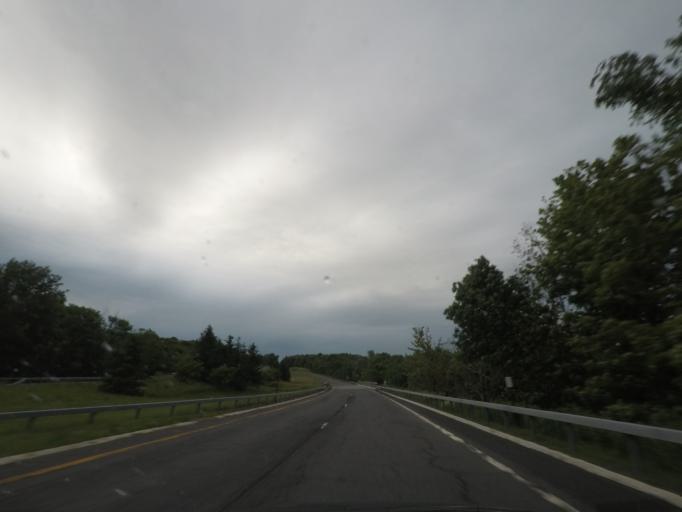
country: US
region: New York
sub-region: Columbia County
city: Chatham
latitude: 42.3320
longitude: -73.5679
